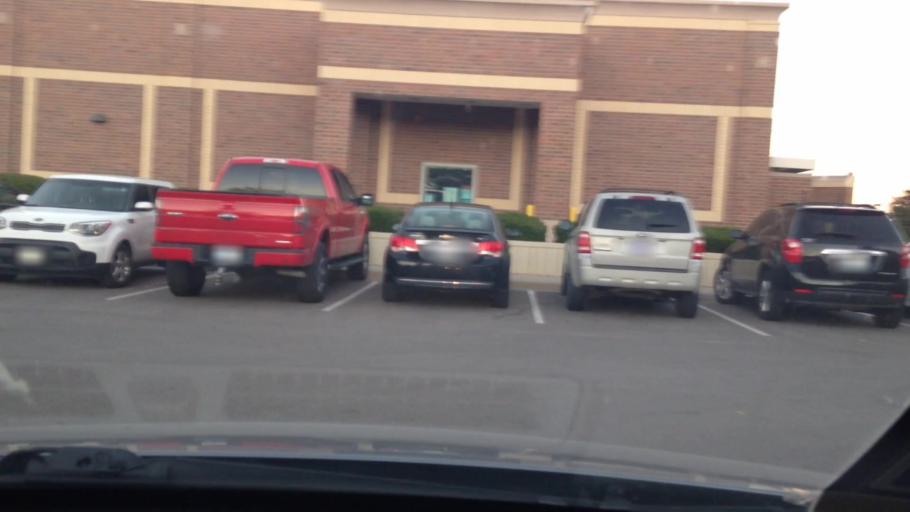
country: US
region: Kansas
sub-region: Johnson County
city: Overland Park
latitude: 38.9561
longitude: -94.6877
